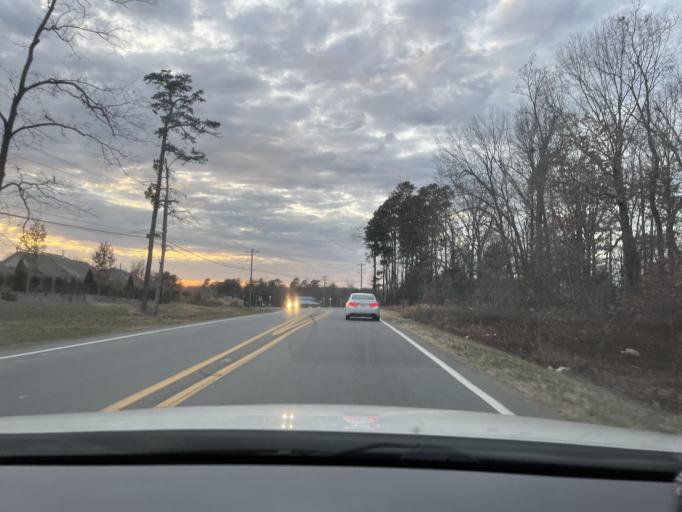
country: US
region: North Carolina
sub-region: Guilford County
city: Gibsonville
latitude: 36.0812
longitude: -79.5374
